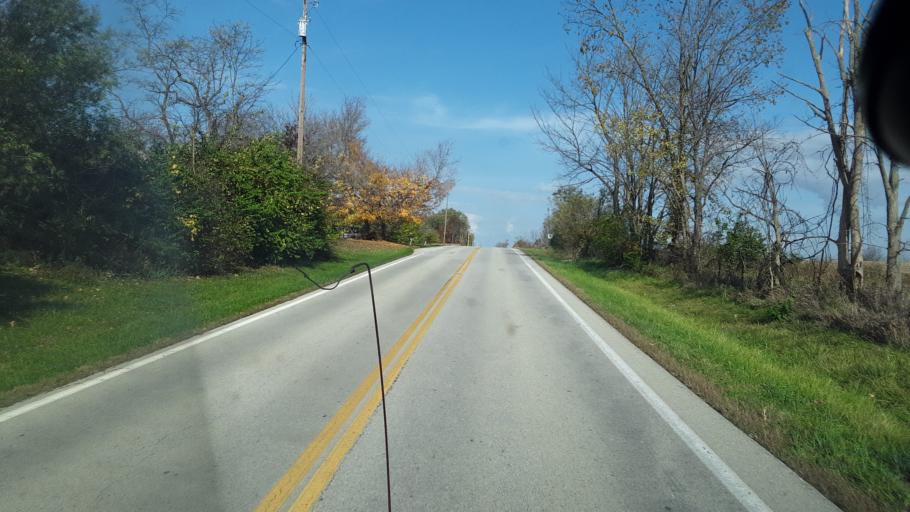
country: US
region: Ohio
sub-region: Clinton County
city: Sabina
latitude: 39.5137
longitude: -83.6909
